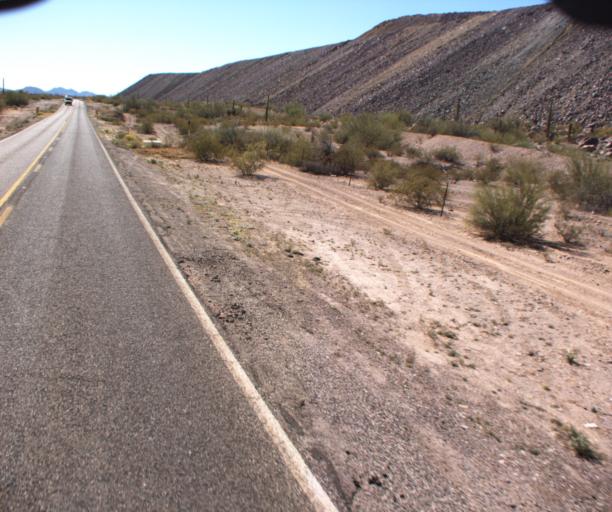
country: US
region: Arizona
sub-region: Pima County
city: Ajo
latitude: 32.3646
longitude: -112.8374
